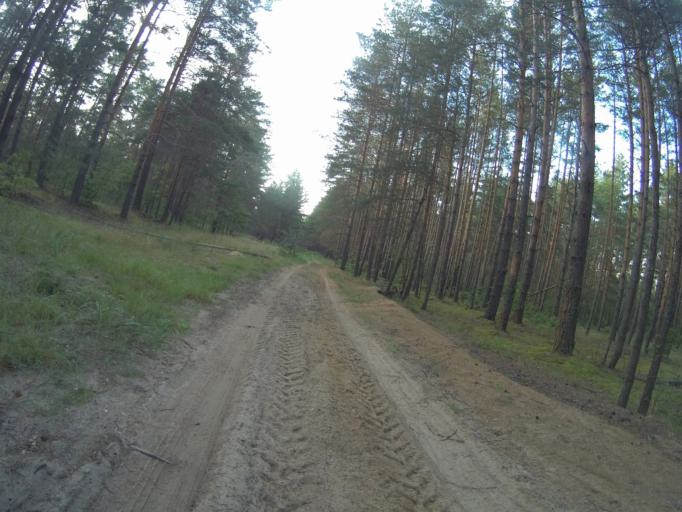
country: RU
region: Vladimir
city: Kommunar
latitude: 56.0821
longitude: 40.4398
